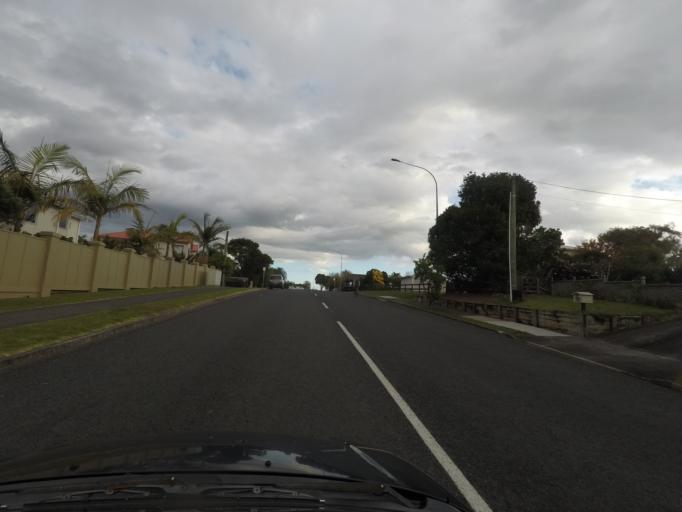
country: NZ
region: Auckland
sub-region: Auckland
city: Rosebank
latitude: -36.8034
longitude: 174.6444
